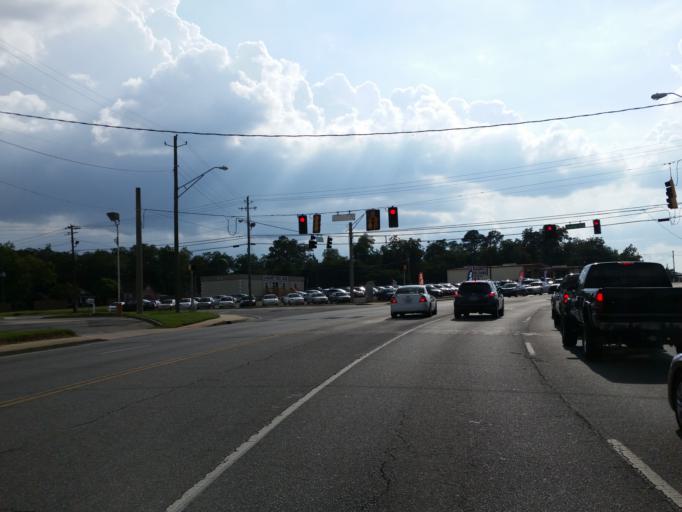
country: US
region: Georgia
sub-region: Tift County
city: Tifton
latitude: 31.4496
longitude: -83.5125
